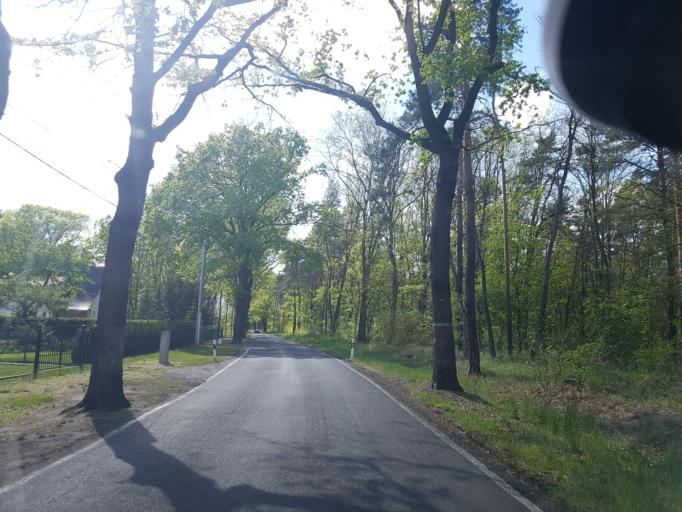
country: DE
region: Brandenburg
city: Cottbus
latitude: 51.6799
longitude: 14.3835
